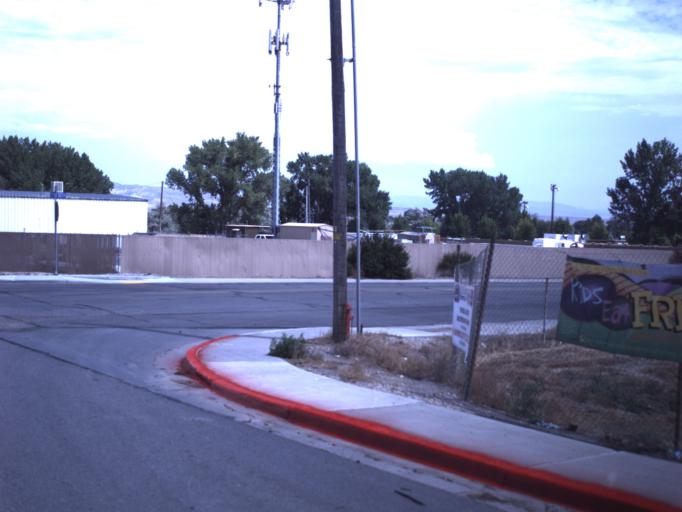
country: US
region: Utah
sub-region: Uintah County
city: Naples
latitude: 40.4284
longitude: -109.4994
